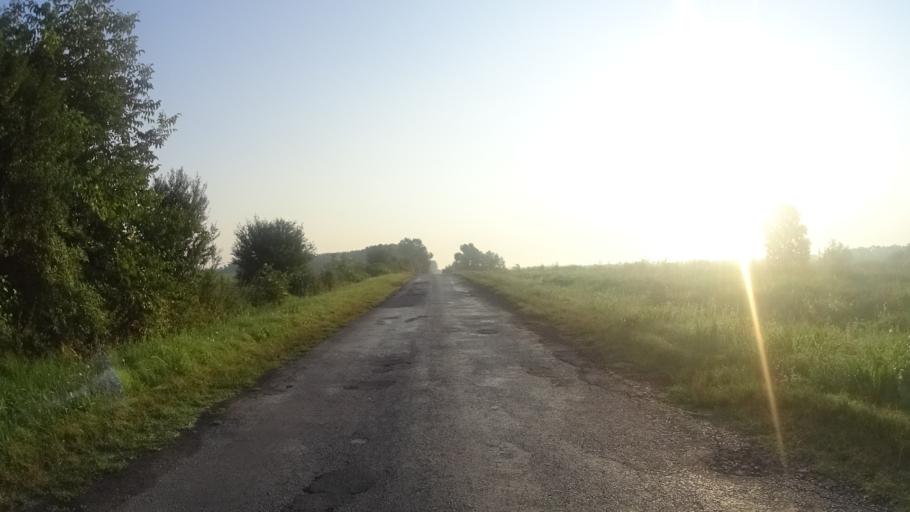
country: HU
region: Zala
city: Zalakomar
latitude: 46.5289
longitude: 17.1363
